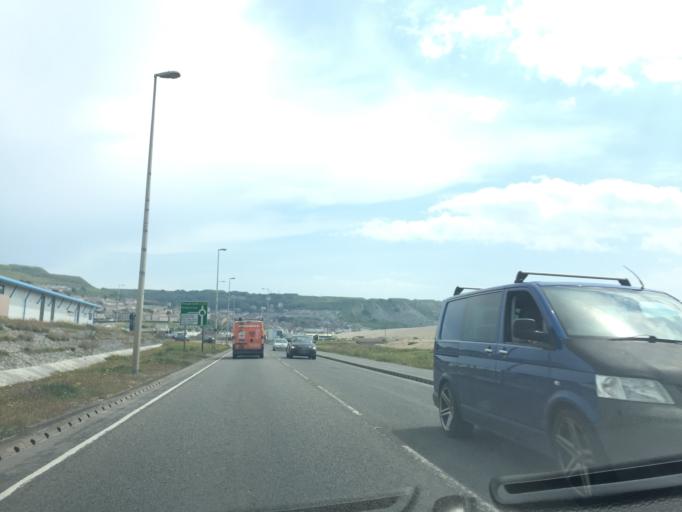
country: GB
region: England
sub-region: Dorset
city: Portland
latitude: 50.5671
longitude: -2.4548
